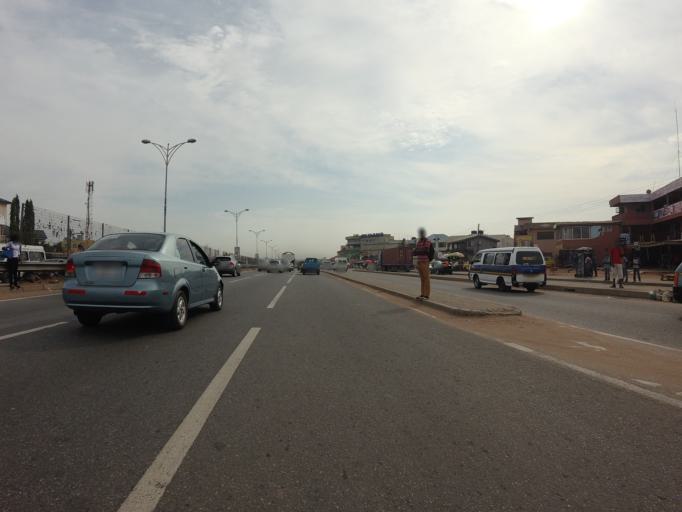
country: GH
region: Greater Accra
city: Dome
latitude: 5.6053
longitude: -0.2519
